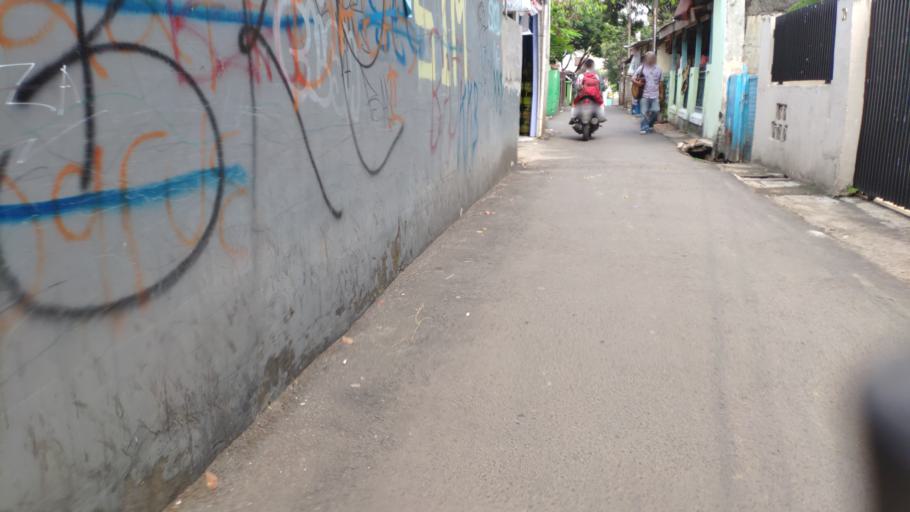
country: ID
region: West Java
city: Depok
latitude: -6.3186
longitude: 106.8258
